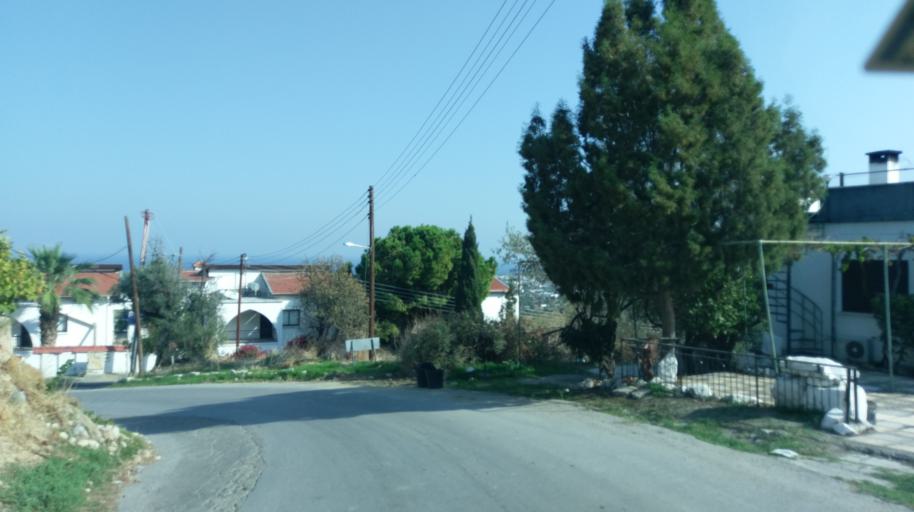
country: CY
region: Keryneia
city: Kyrenia
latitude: 35.3295
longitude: 33.2606
